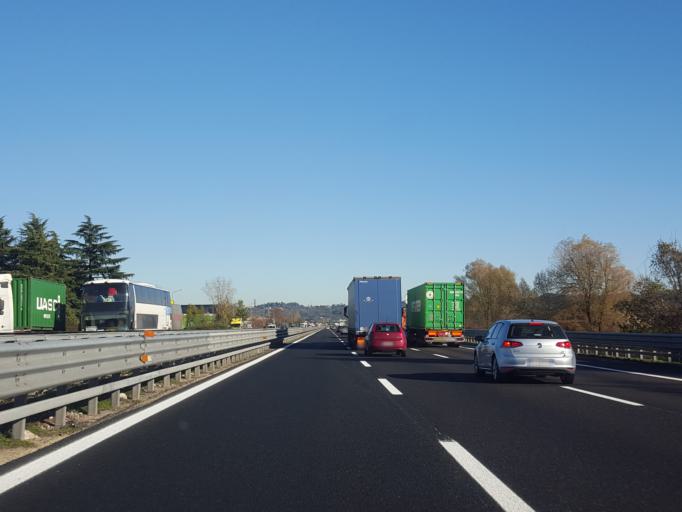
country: IT
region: Veneto
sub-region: Provincia di Vicenza
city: Altavilla Vicentina
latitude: 45.5115
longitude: 11.4833
